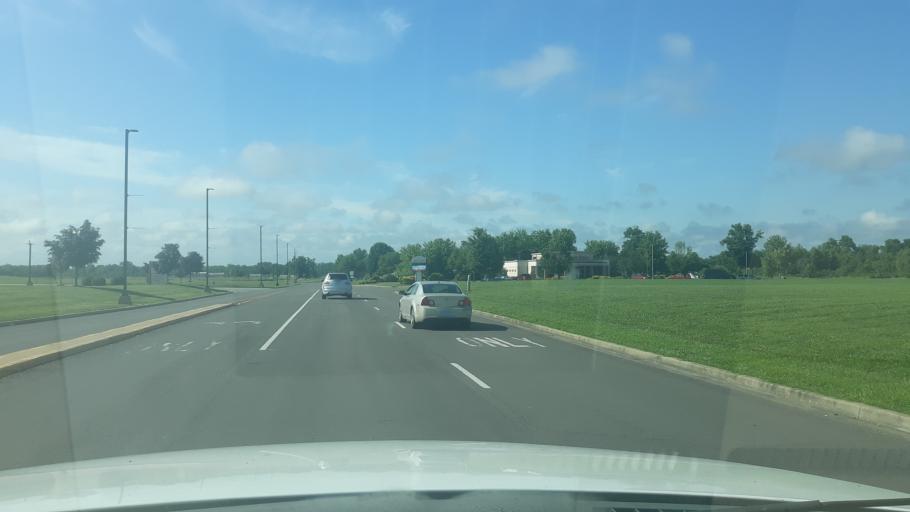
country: US
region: Illinois
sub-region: Williamson County
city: Energy
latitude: 37.7441
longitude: -88.9934
